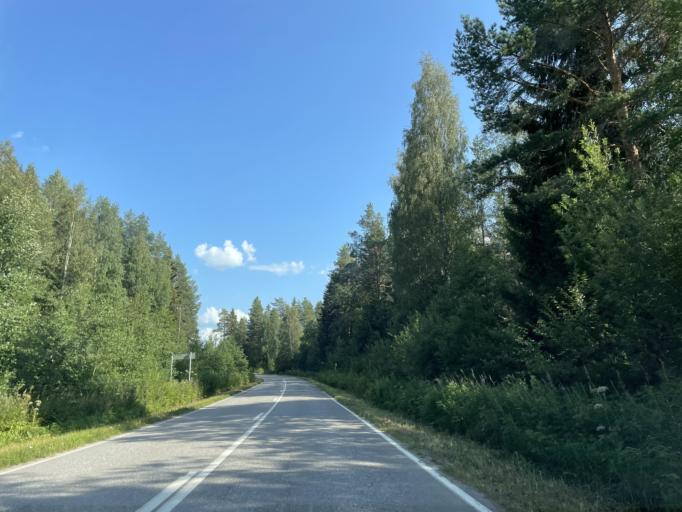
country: FI
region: Central Finland
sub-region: Saarijaervi-Viitasaari
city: Pihtipudas
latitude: 63.3561
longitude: 25.7574
